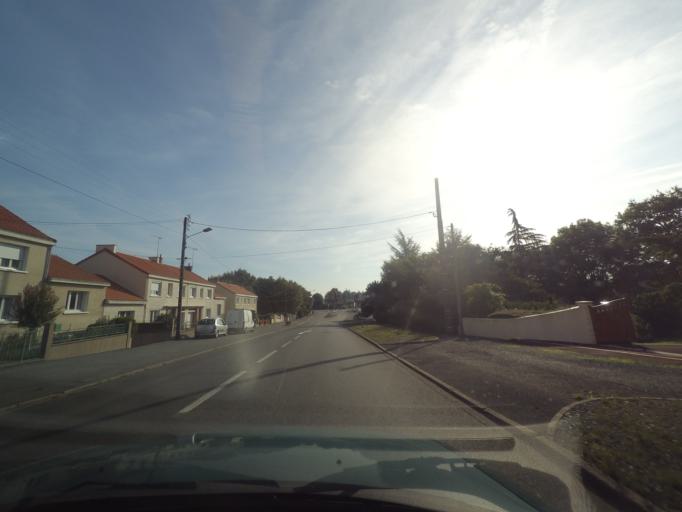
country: FR
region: Pays de la Loire
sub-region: Departement de Maine-et-Loire
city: La Romagne
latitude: 47.0597
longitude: -1.0132
